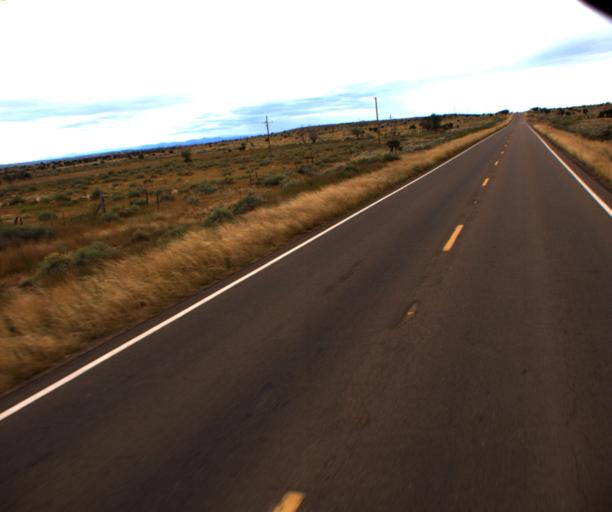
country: US
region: Arizona
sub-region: Navajo County
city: Snowflake
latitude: 34.5591
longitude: -110.0813
